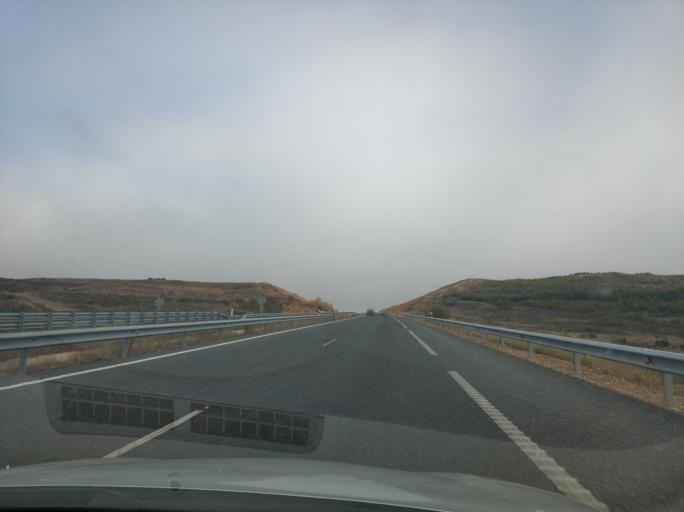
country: ES
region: Castille and Leon
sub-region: Provincia de Leon
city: Leon
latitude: 42.5638
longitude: -5.5349
